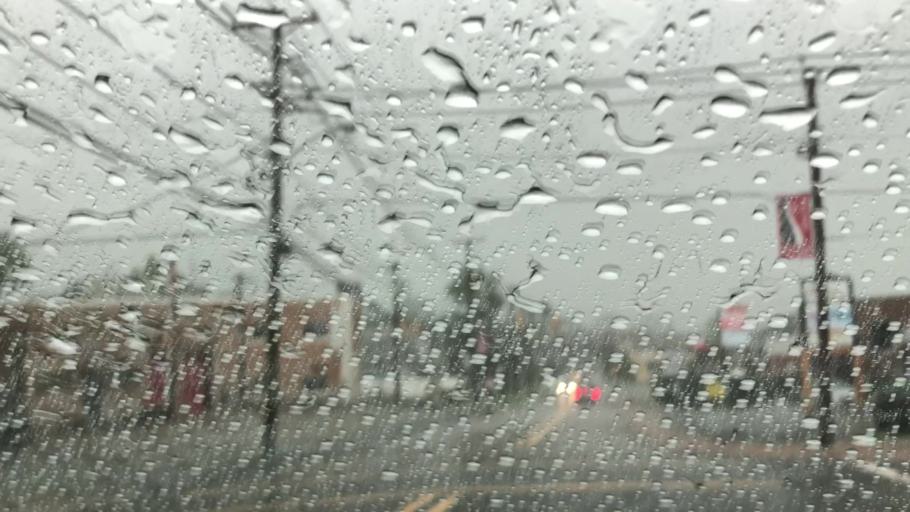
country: US
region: New Jersey
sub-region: Bergen County
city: Saddle Brook
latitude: 40.8954
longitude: -74.0823
